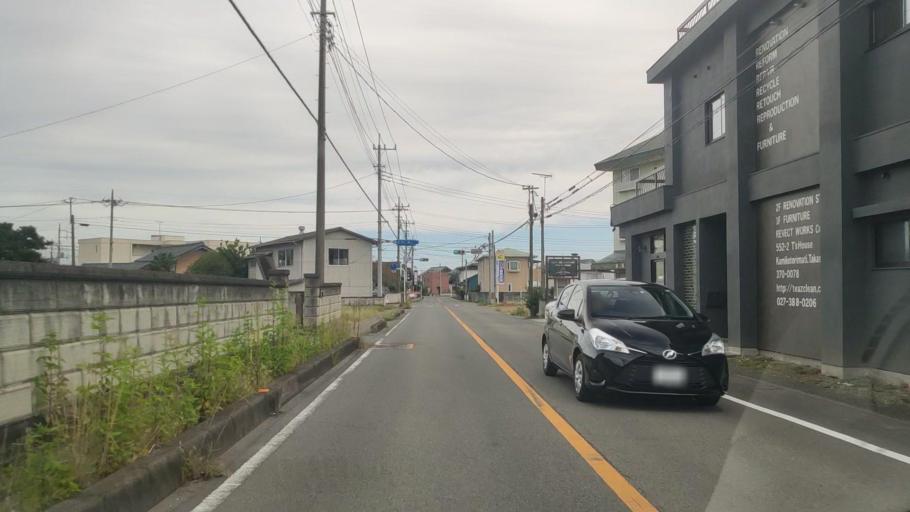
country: JP
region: Gunma
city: Takasaki
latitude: 36.3601
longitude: 138.9858
